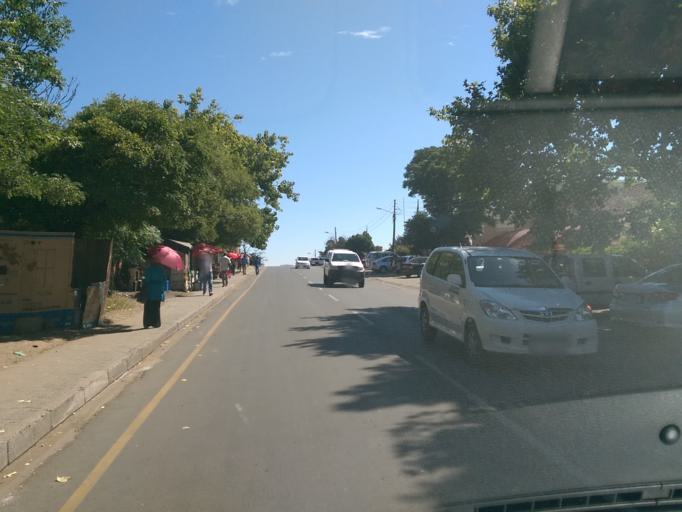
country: LS
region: Maseru
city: Maseru
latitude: -29.3135
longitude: 27.4840
